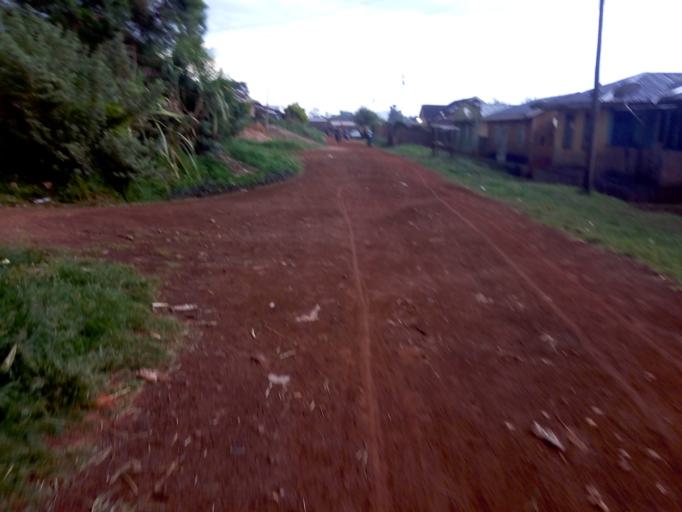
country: UG
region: Western Region
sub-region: Masindi District
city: Masindi
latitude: 1.6820
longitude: 31.7165
